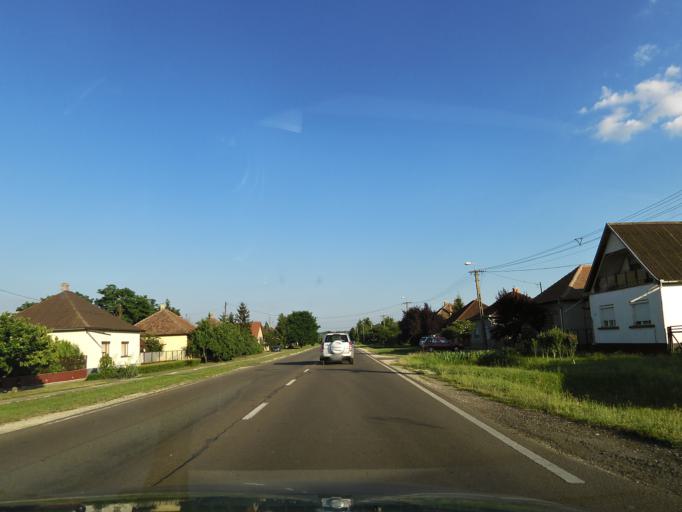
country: HU
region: Jasz-Nagykun-Szolnok
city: Rakocziujfalu
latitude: 47.0567
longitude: 20.2644
